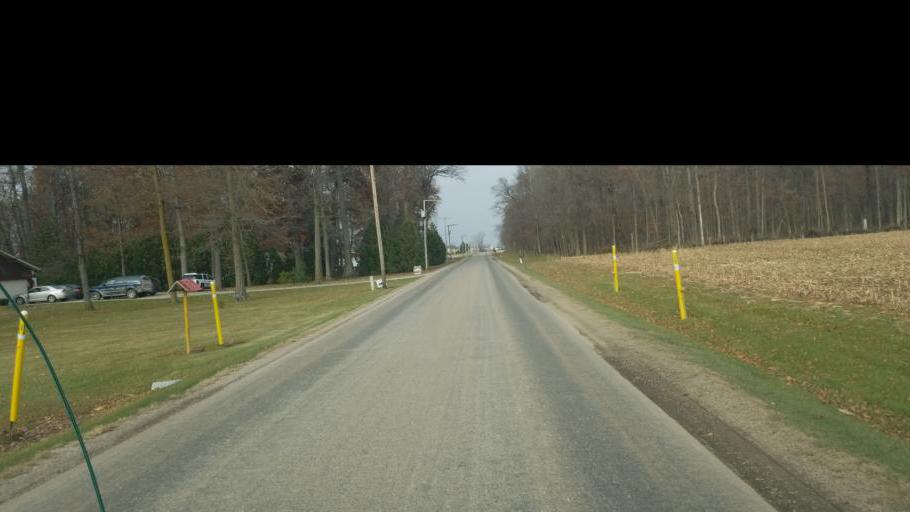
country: US
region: Indiana
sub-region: Adams County
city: Berne
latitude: 40.6502
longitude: -84.9358
